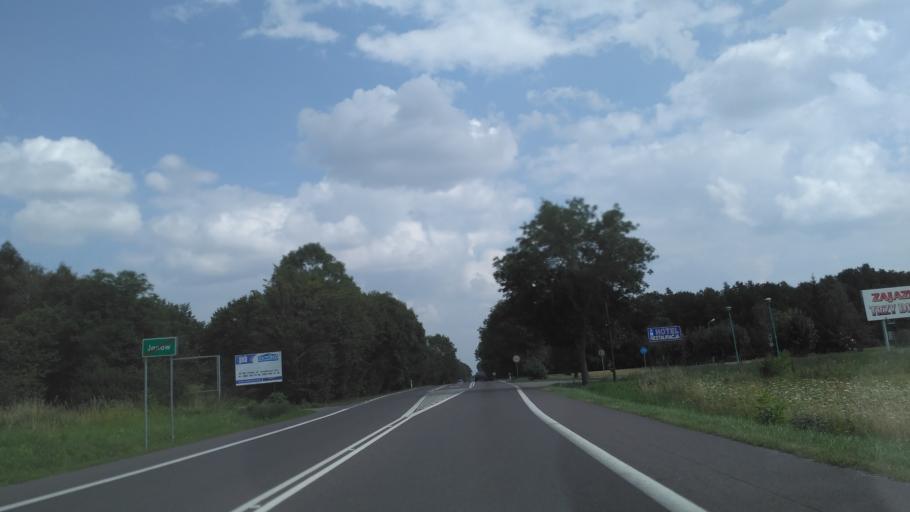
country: PL
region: Lublin Voivodeship
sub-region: Chelm
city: Chelm
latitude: 51.1592
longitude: 23.3984
